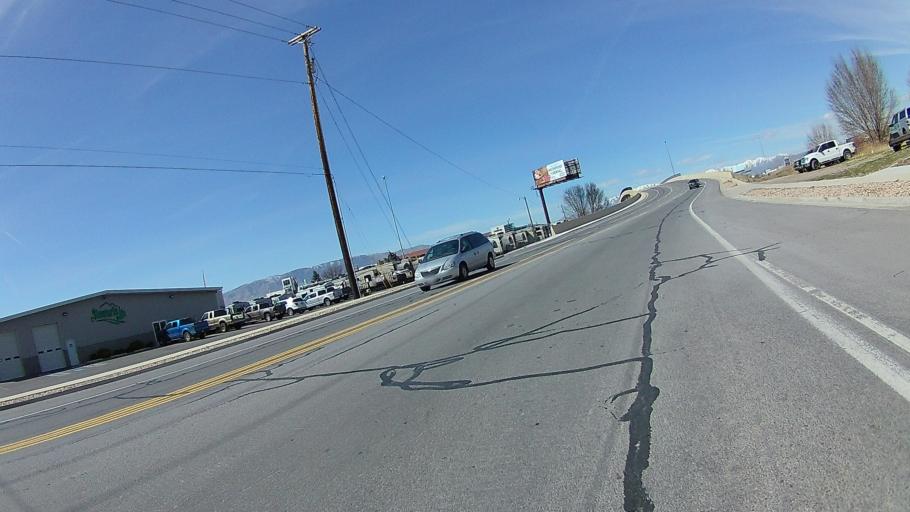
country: US
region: Utah
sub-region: Utah County
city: American Fork
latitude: 40.3554
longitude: -111.7744
